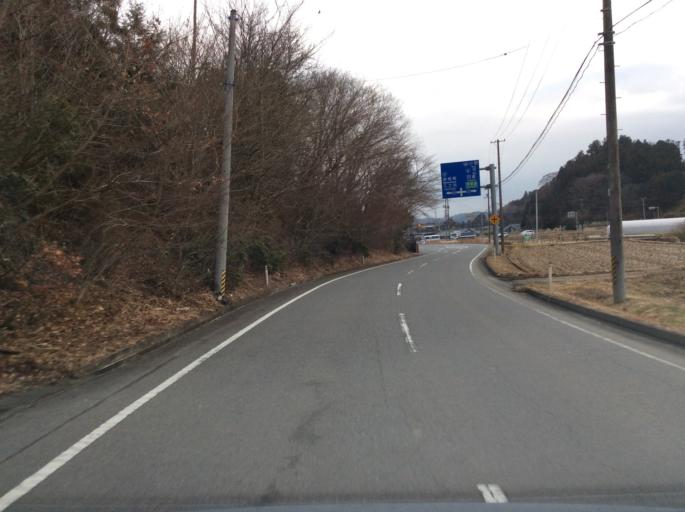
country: JP
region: Fukushima
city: Iwaki
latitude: 37.1306
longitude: 140.9537
